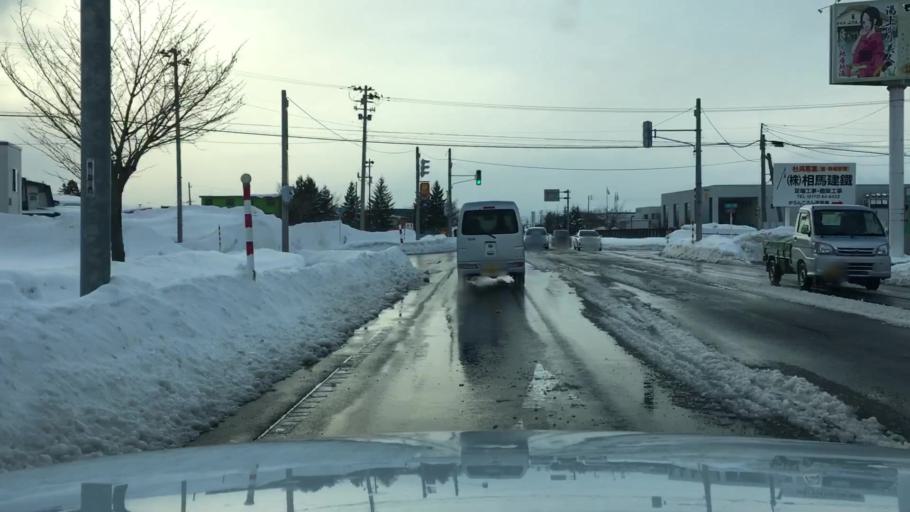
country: JP
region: Aomori
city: Hirosaki
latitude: 40.5945
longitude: 140.5358
